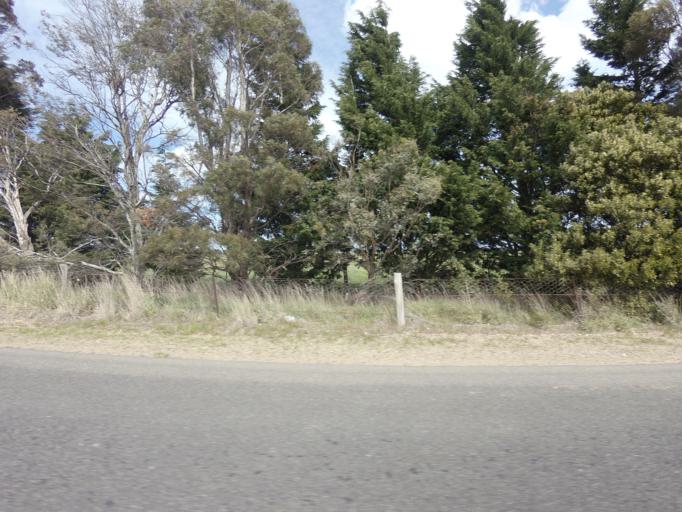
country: AU
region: Tasmania
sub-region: Northern Midlands
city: Longford
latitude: -41.6610
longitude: 147.1717
